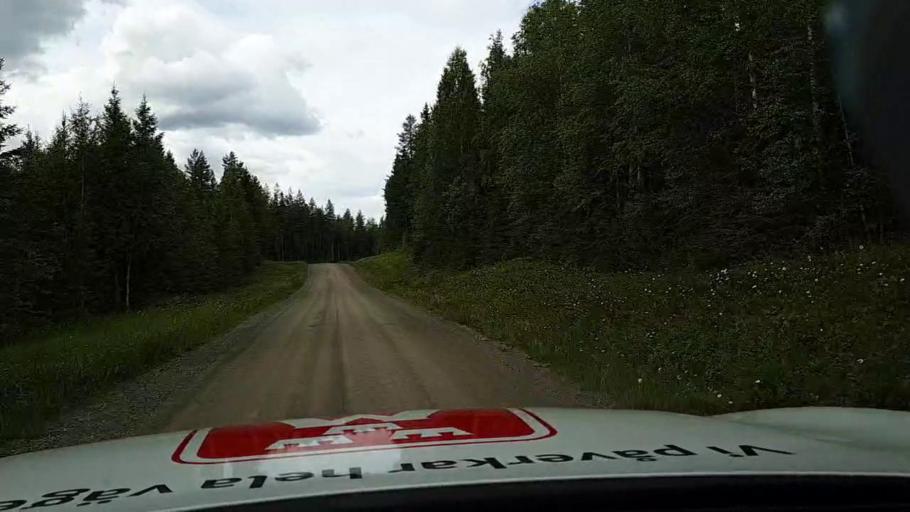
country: SE
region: Jaemtland
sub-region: Stroemsunds Kommun
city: Stroemsund
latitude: 63.3224
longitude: 15.4713
